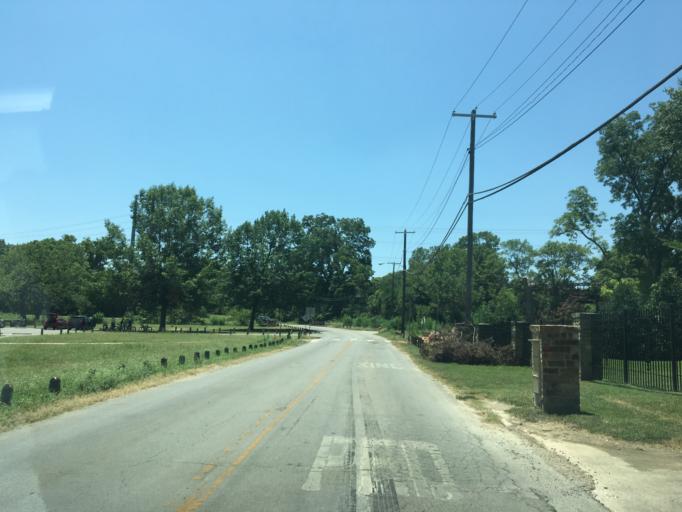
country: US
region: Texas
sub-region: Dallas County
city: Highland Park
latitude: 32.8323
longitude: -96.7323
